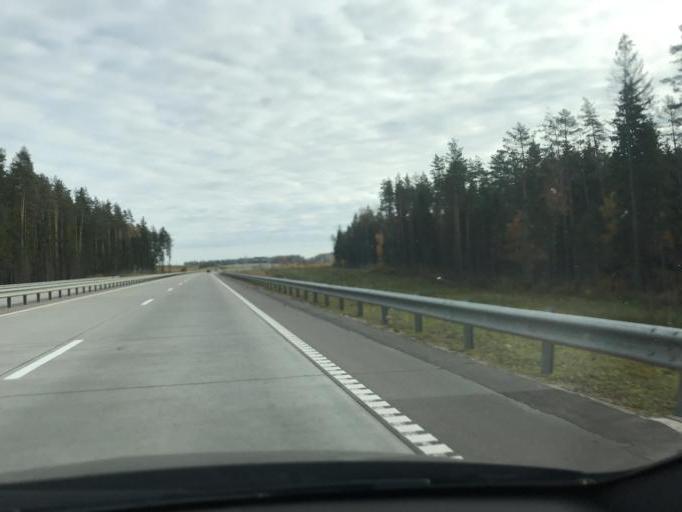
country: BY
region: Minsk
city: Syomkava
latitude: 54.0634
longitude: 27.3817
